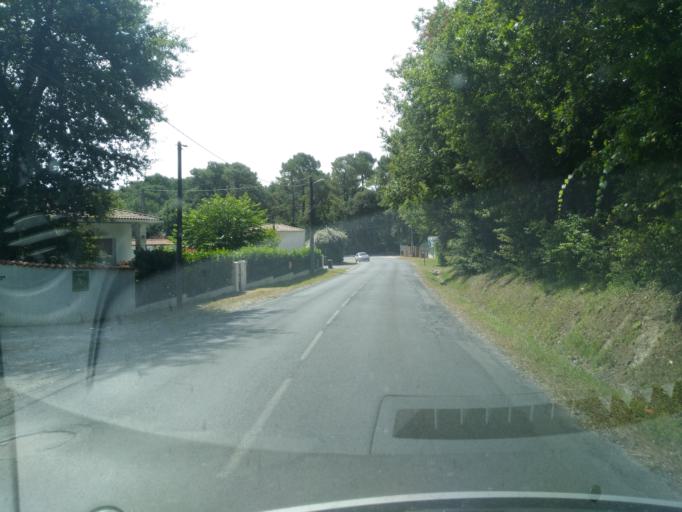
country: FR
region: Poitou-Charentes
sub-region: Departement de la Charente-Maritime
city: Saint-Palais-sur-Mer
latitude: 45.6664
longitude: -1.0793
